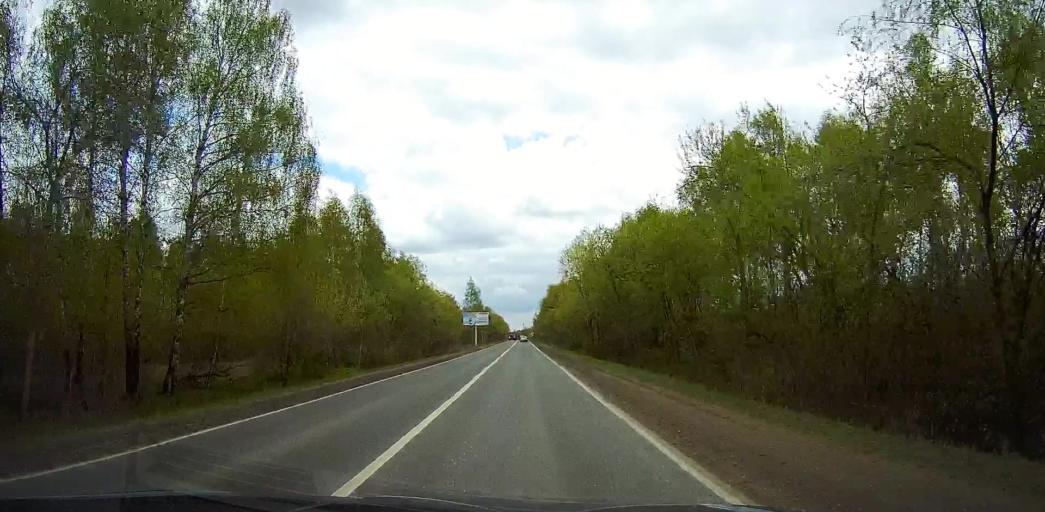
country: RU
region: Moskovskaya
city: Ashitkovo
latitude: 55.4325
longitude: 38.5328
